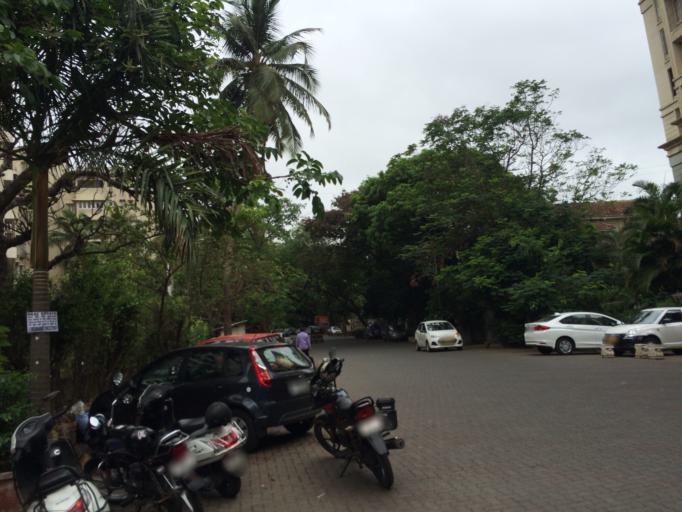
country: IN
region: Maharashtra
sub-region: Mumbai Suburban
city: Mumbai
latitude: 19.0485
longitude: 72.8225
